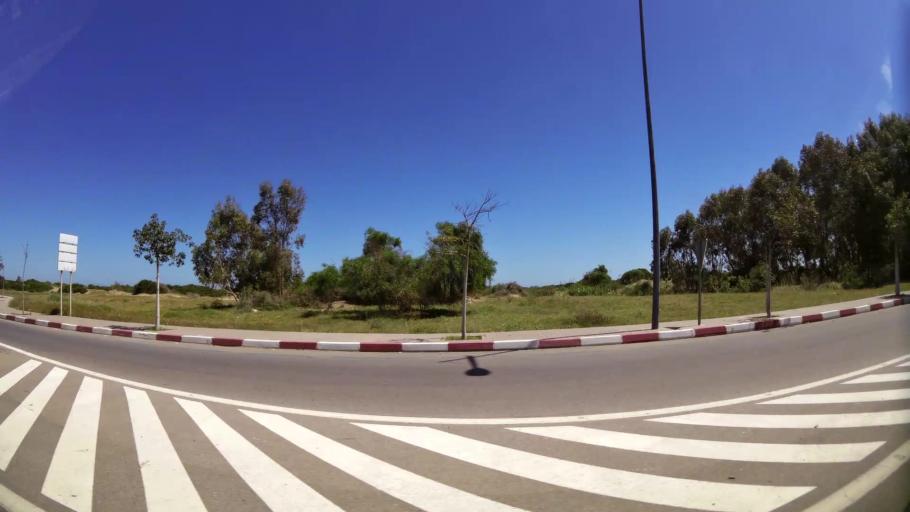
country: MA
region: Oriental
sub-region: Berkane-Taourirt
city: Madagh
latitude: 35.0940
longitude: -2.2587
